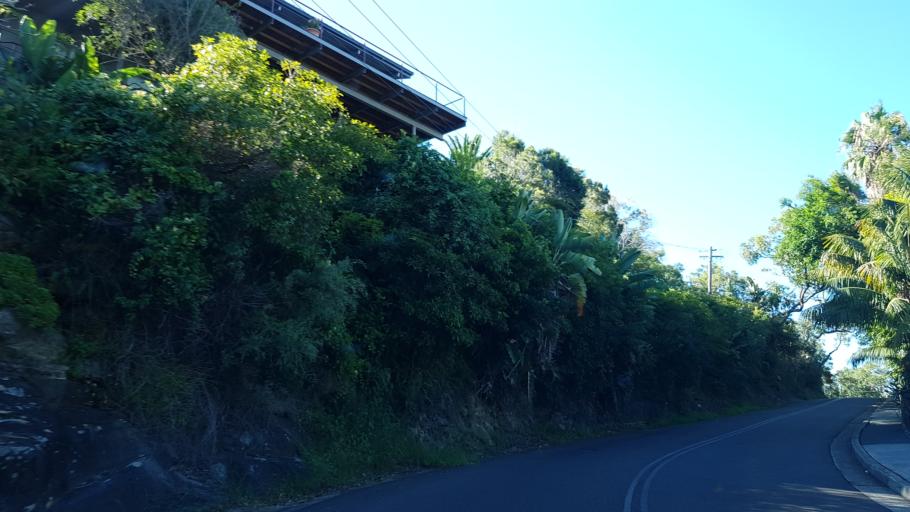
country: AU
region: New South Wales
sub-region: Pittwater
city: Palm Beach
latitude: -33.6161
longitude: 151.3318
